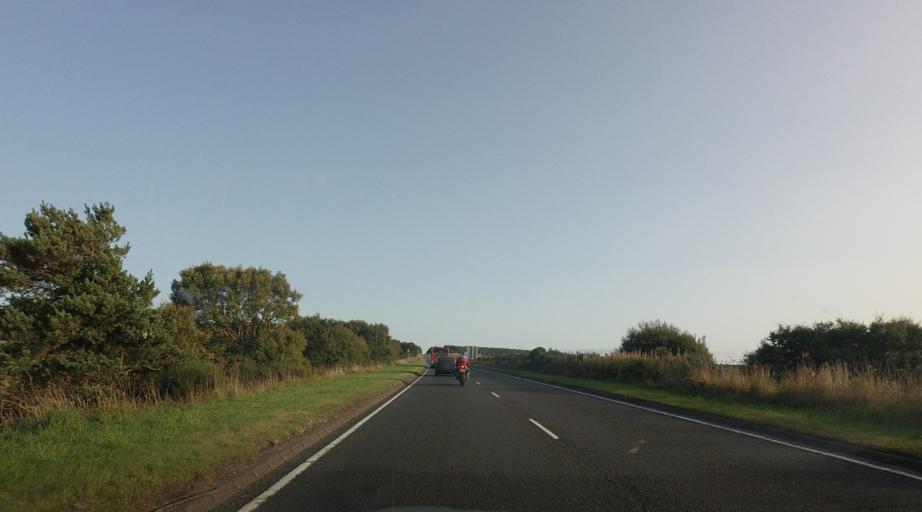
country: GB
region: Scotland
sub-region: Highland
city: Dingwall
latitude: 57.5745
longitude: -4.3548
